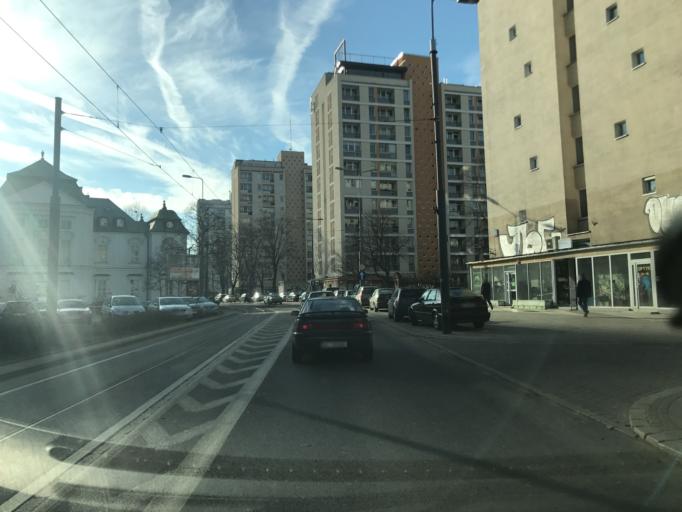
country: PL
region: Masovian Voivodeship
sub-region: Warszawa
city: Warsaw
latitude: 52.2459
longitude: 21.0054
